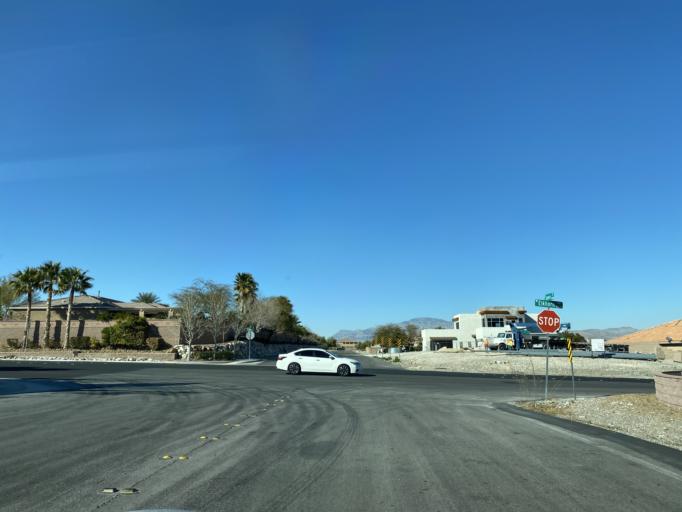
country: US
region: Nevada
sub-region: Clark County
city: Summerlin South
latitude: 36.2916
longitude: -115.3081
